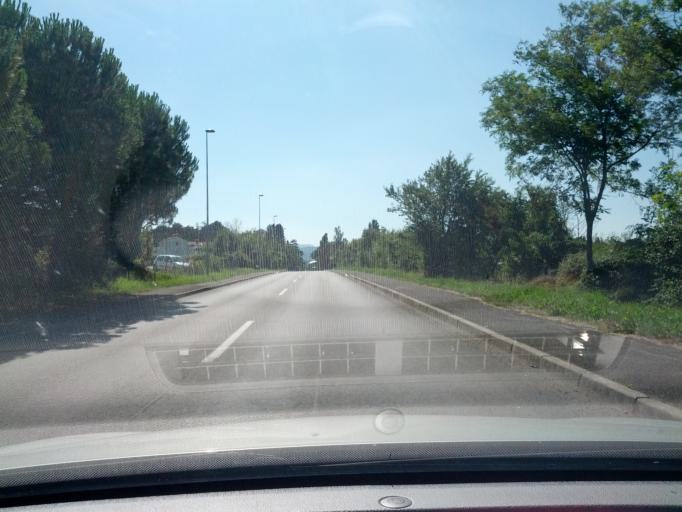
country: SI
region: Koper-Capodistria
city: Ankaran
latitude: 45.5727
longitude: 13.7458
